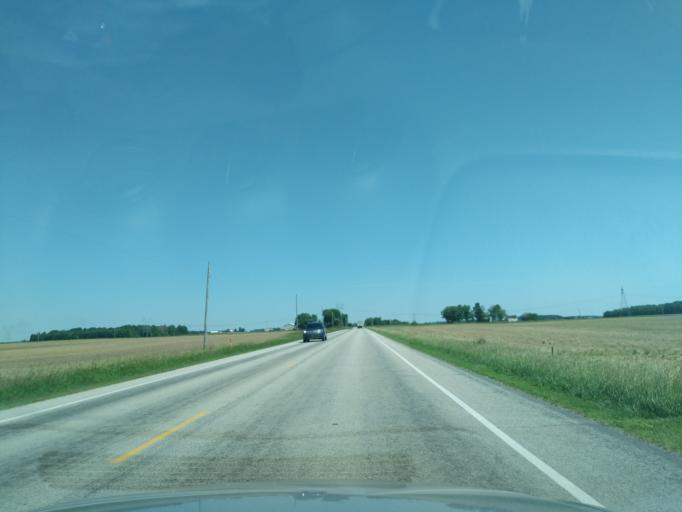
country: US
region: Indiana
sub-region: Huntington County
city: Huntington
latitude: 40.9277
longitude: -85.4710
